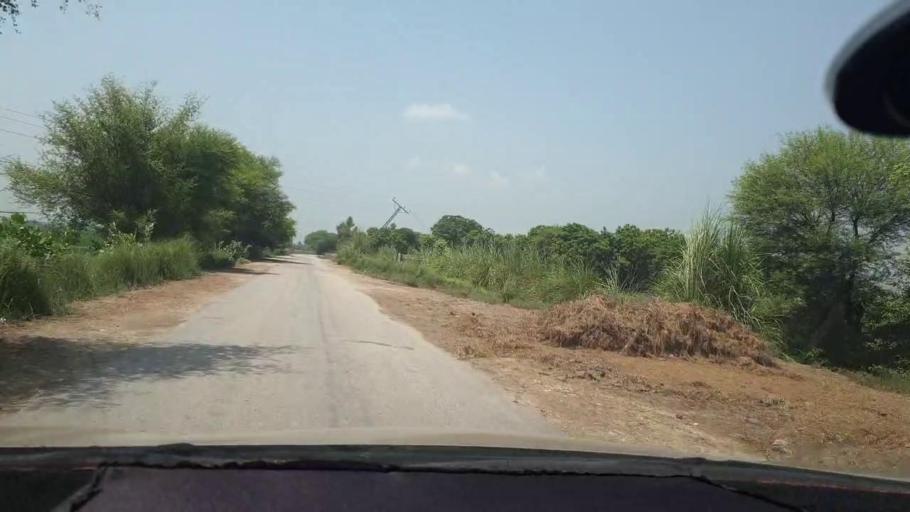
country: PK
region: Sindh
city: Kambar
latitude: 27.6629
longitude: 67.9297
